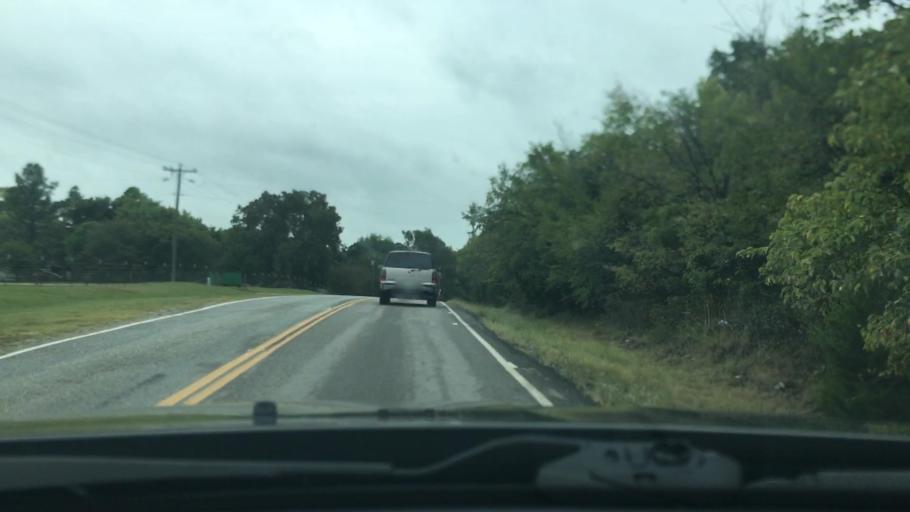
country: US
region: Oklahoma
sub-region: Pontotoc County
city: Ada
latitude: 34.6018
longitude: -96.6348
